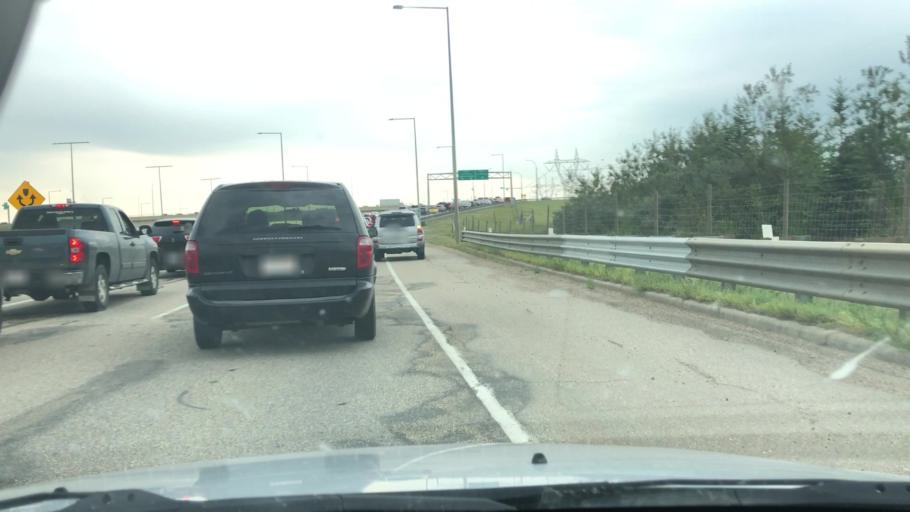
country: CA
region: Alberta
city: Edmonton
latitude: 53.4352
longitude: -113.5141
